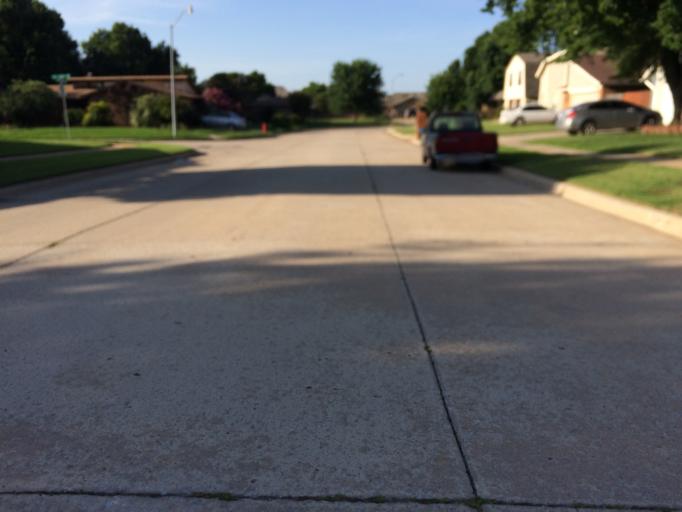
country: US
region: Oklahoma
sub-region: Cleveland County
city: Norman
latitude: 35.2256
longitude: -97.4882
